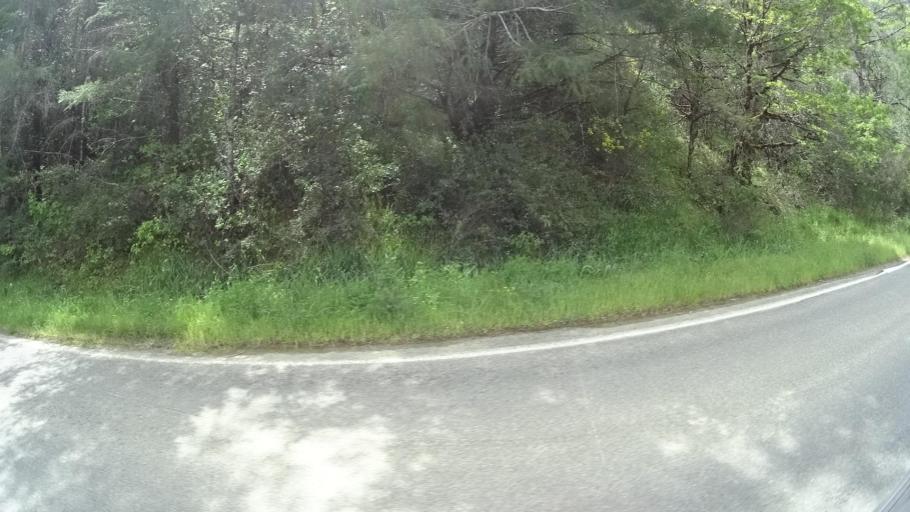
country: US
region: California
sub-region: Humboldt County
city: Redway
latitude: 40.1299
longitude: -123.8597
